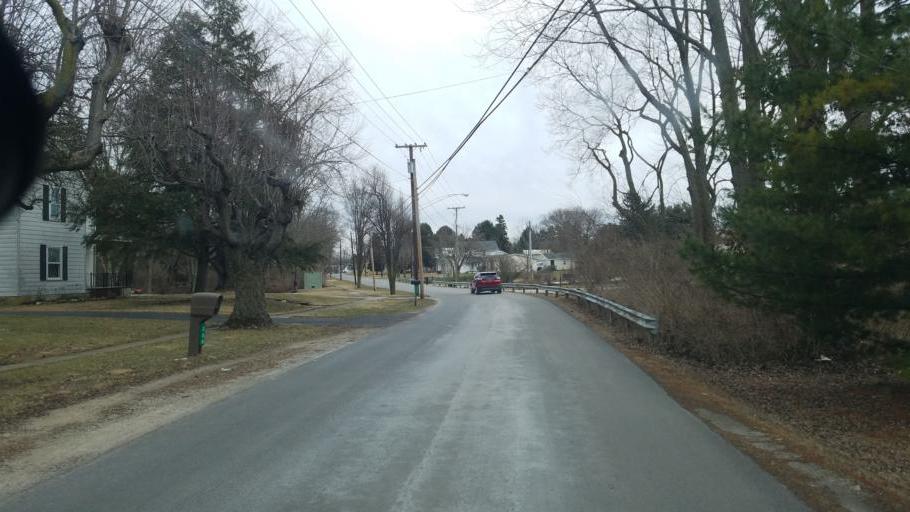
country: US
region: Ohio
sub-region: Marion County
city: Prospect
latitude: 40.4579
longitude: -83.0839
